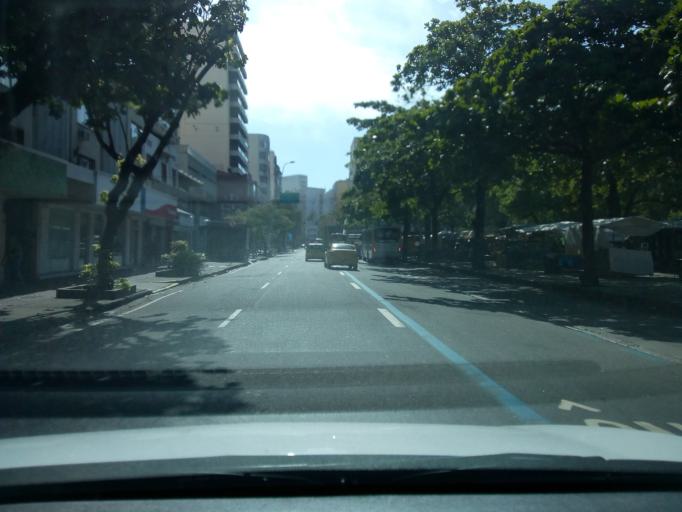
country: BR
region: Rio de Janeiro
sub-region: Rio De Janeiro
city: Rio de Janeiro
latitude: -22.9847
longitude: -43.1984
